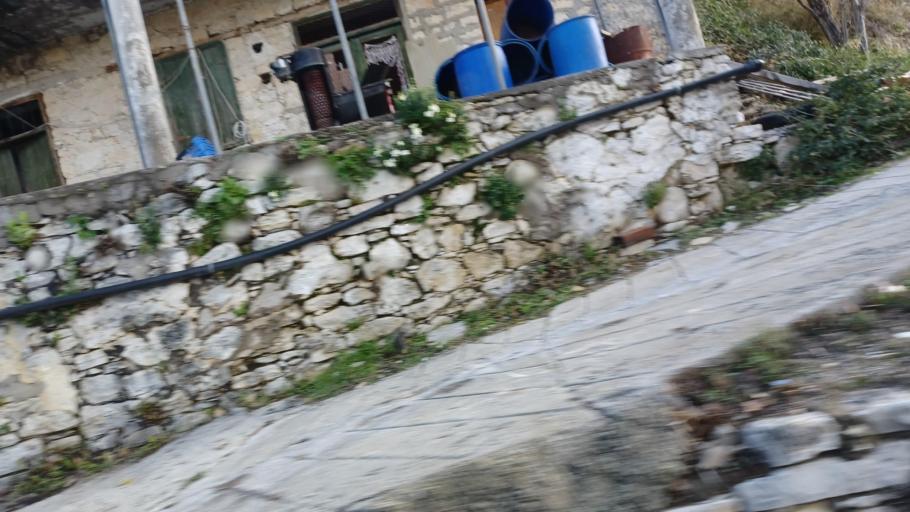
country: CY
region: Limassol
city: Pachna
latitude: 34.8689
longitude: 32.6910
